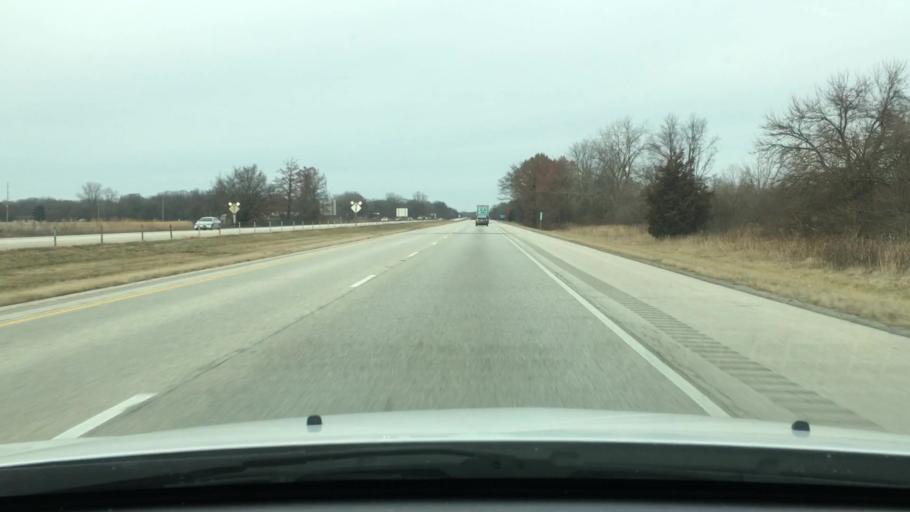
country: US
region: Illinois
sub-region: Sangamon County
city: Grandview
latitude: 39.8503
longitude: -89.5945
